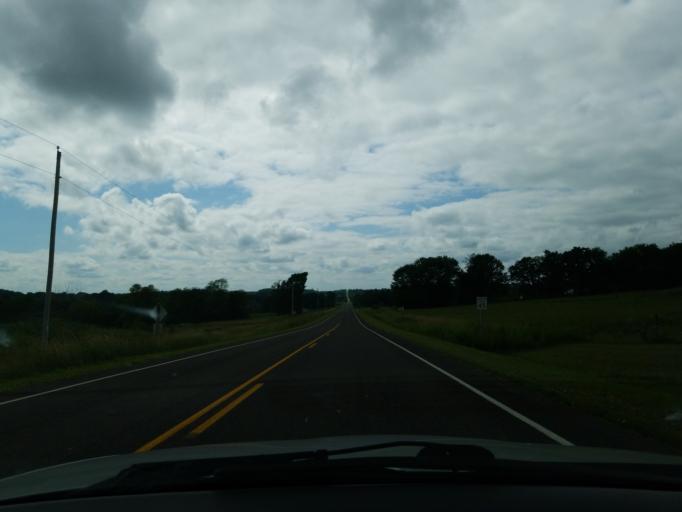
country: US
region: Wisconsin
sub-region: Saint Croix County
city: Glenwood City
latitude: 44.9881
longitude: -92.1789
